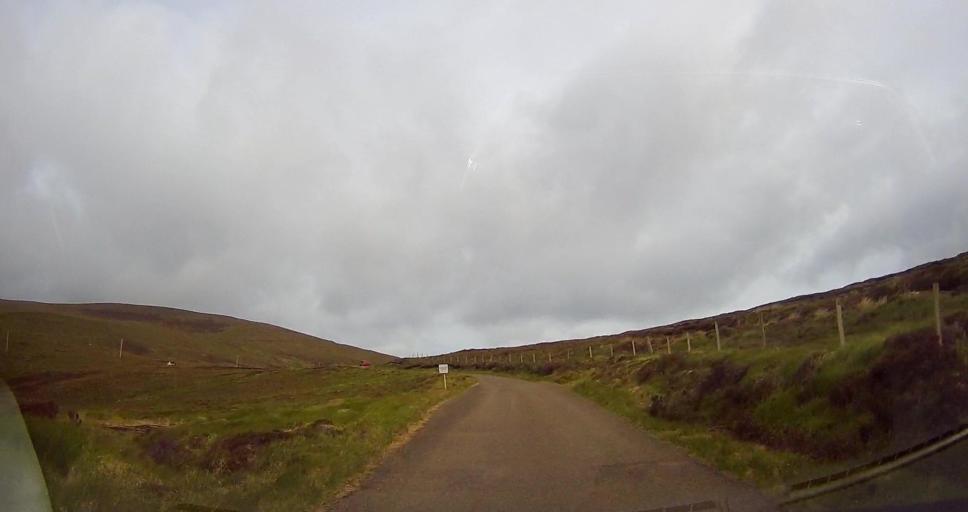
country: GB
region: Scotland
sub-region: Orkney Islands
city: Stromness
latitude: 58.8779
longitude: -3.2470
